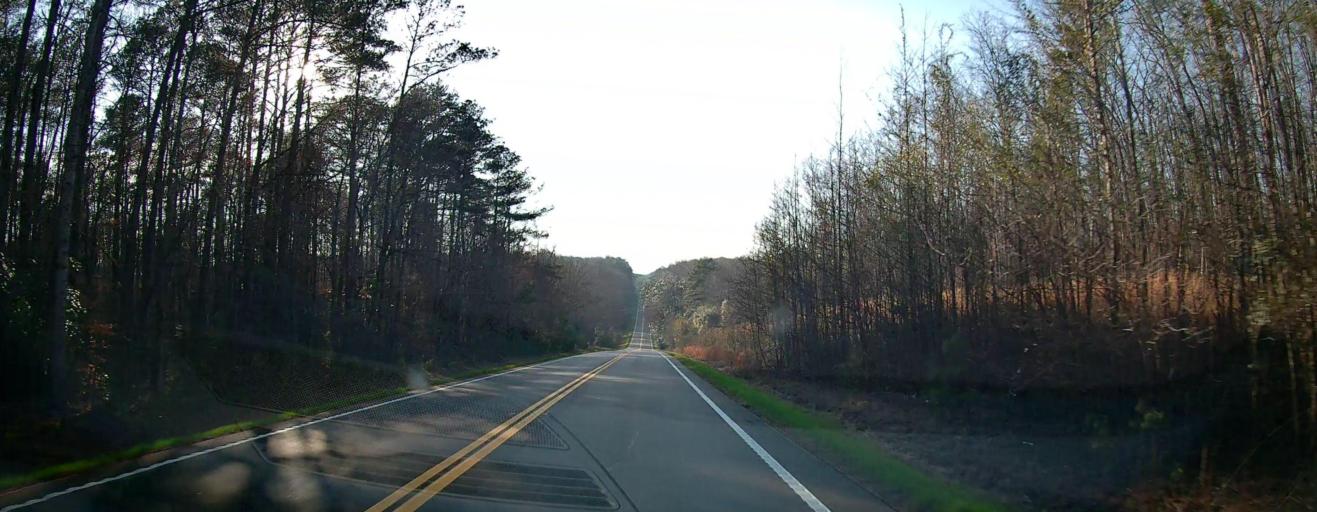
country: US
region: Georgia
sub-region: Harris County
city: Hamilton
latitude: 32.7403
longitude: -84.9608
